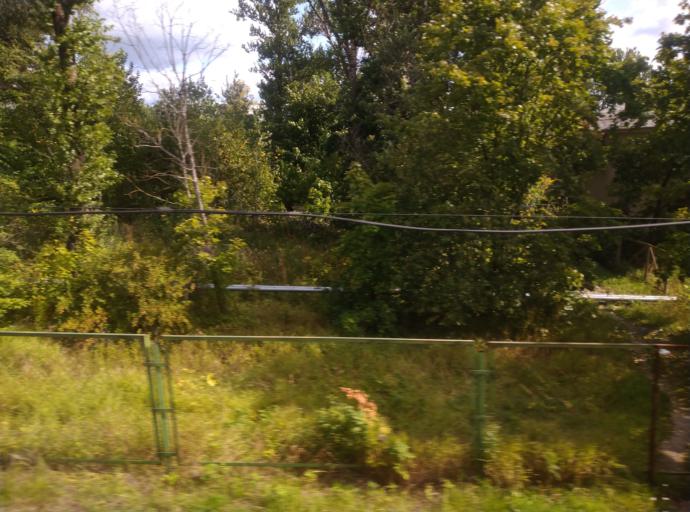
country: RU
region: Leningrad
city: Ul'yanovka
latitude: 59.6378
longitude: 30.7543
